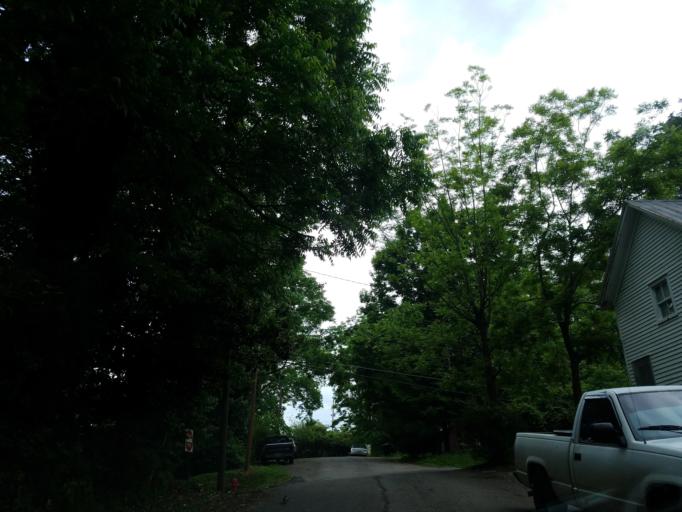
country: US
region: Georgia
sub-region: Lumpkin County
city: Dahlonega
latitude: 34.5328
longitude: -83.9805
